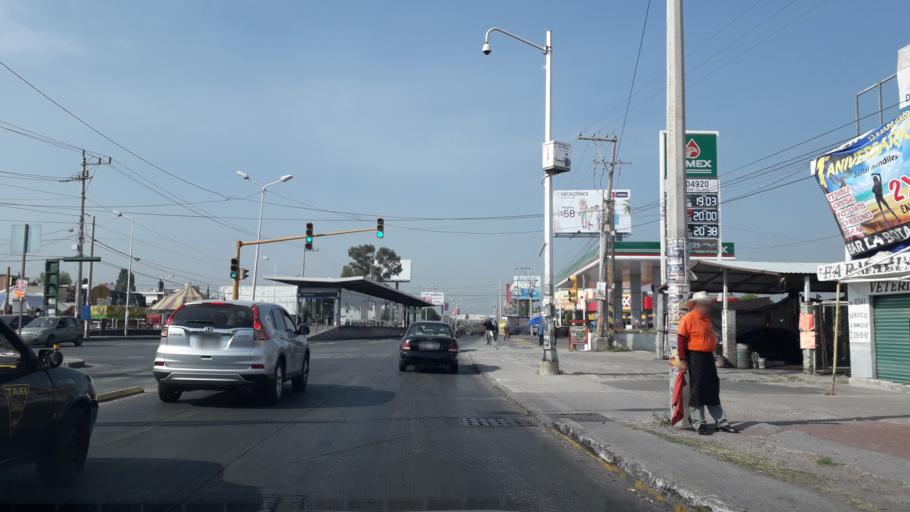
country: MX
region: Puebla
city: Tlazcalancingo
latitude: 18.9983
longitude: -98.2405
